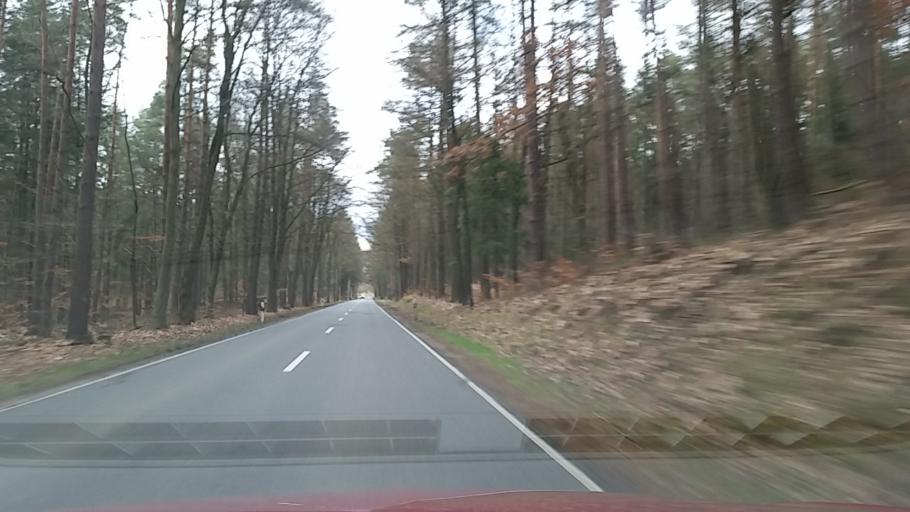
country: DE
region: Lower Saxony
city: Zernien
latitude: 53.1074
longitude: 10.9453
